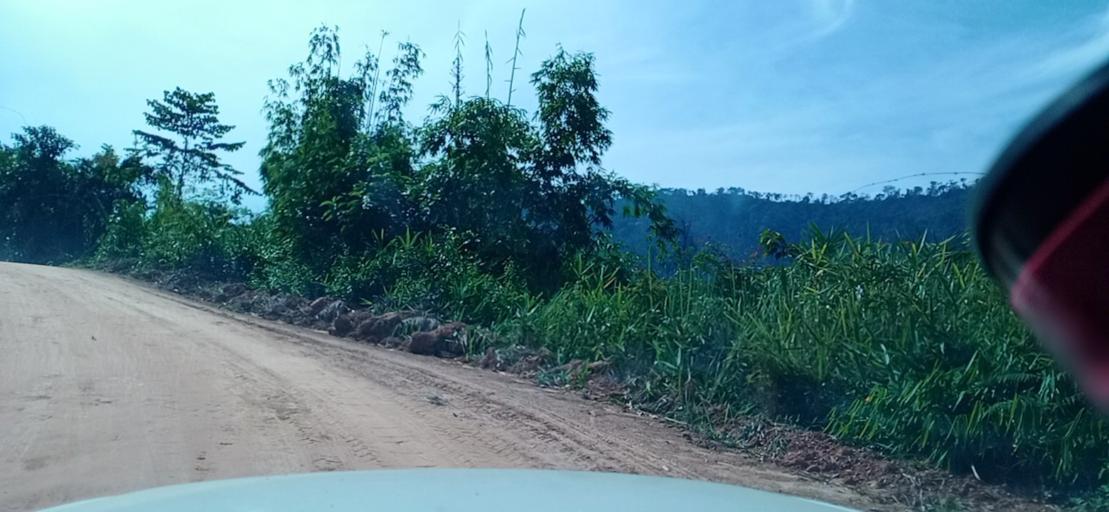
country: TH
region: Changwat Bueng Kan
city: Pak Khat
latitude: 18.6377
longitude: 103.2463
